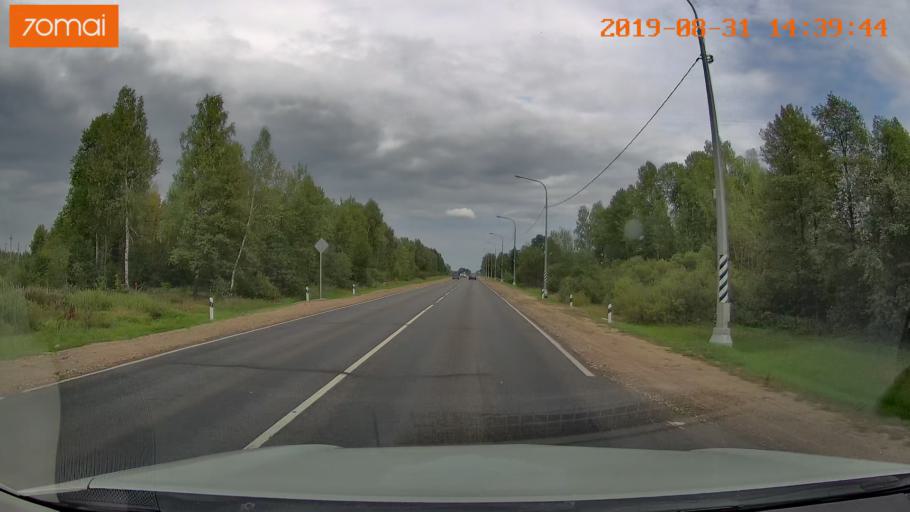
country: RU
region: Smolensk
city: Yekimovichi
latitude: 54.1936
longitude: 33.5592
